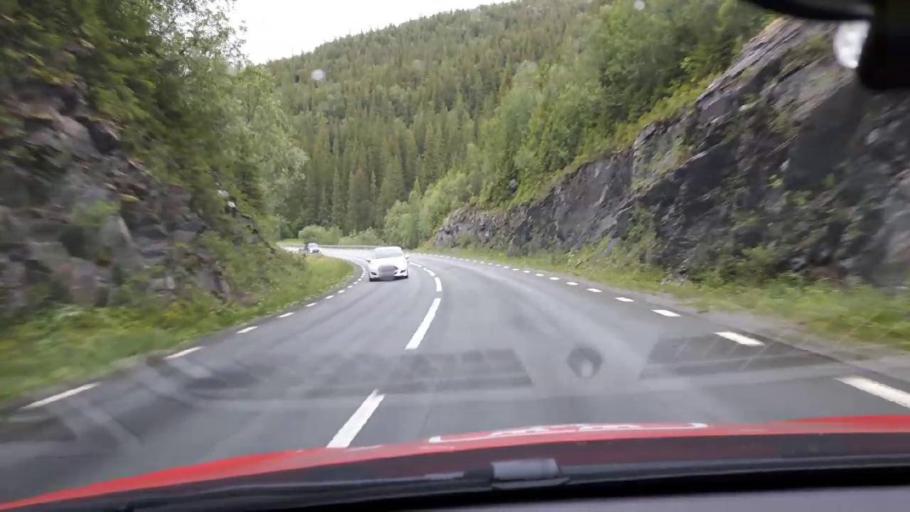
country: NO
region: Nord-Trondelag
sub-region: Meraker
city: Meraker
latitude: 63.3339
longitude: 12.0620
